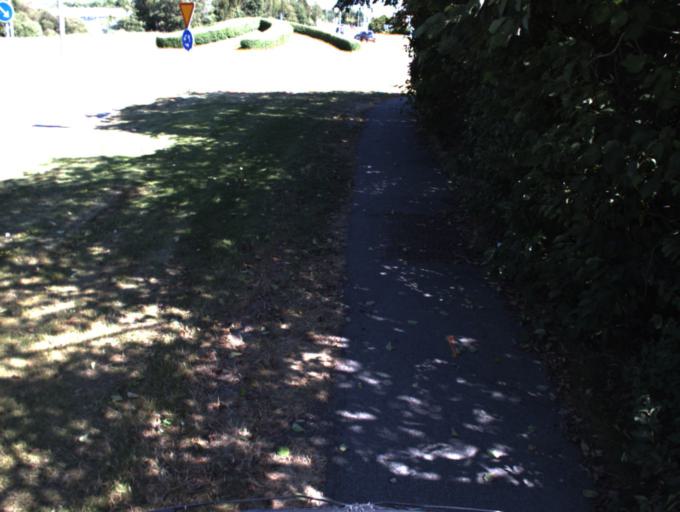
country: SE
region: Skane
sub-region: Helsingborg
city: Odakra
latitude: 56.0813
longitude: 12.7306
